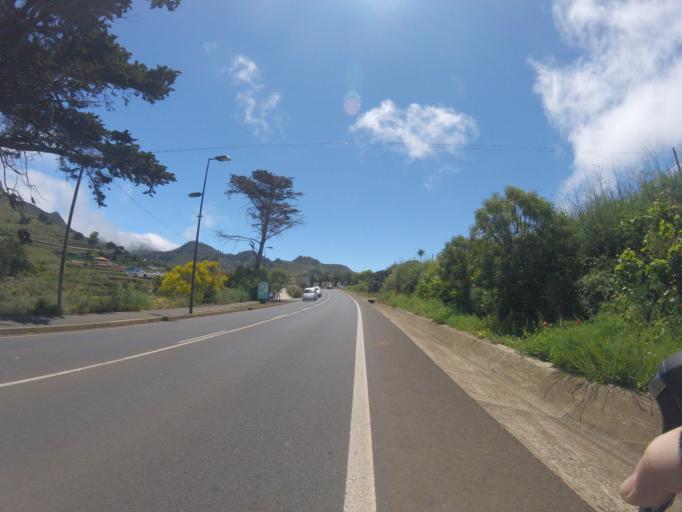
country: ES
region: Canary Islands
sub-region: Provincia de Santa Cruz de Tenerife
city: Tegueste
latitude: 28.5187
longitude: -16.3259
